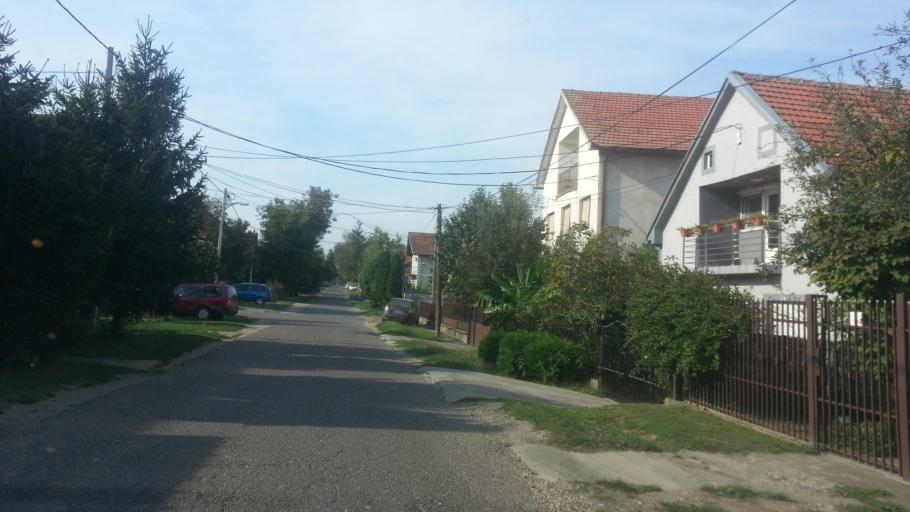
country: RS
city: Novi Banovci
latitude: 44.9504
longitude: 20.2807
